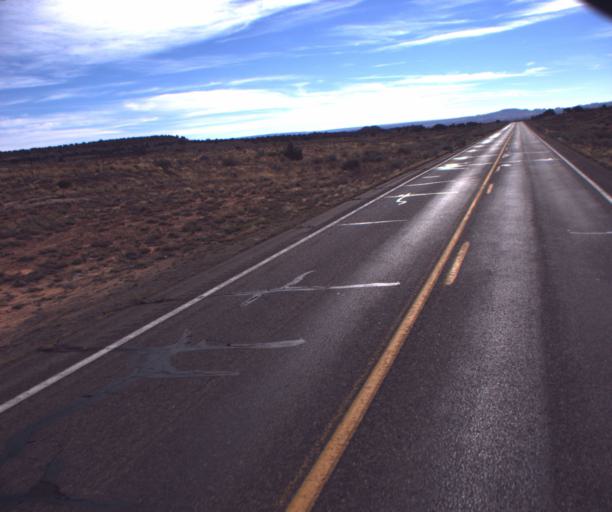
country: US
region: Arizona
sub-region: Coconino County
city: Kaibito
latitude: 36.6683
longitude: -111.2543
